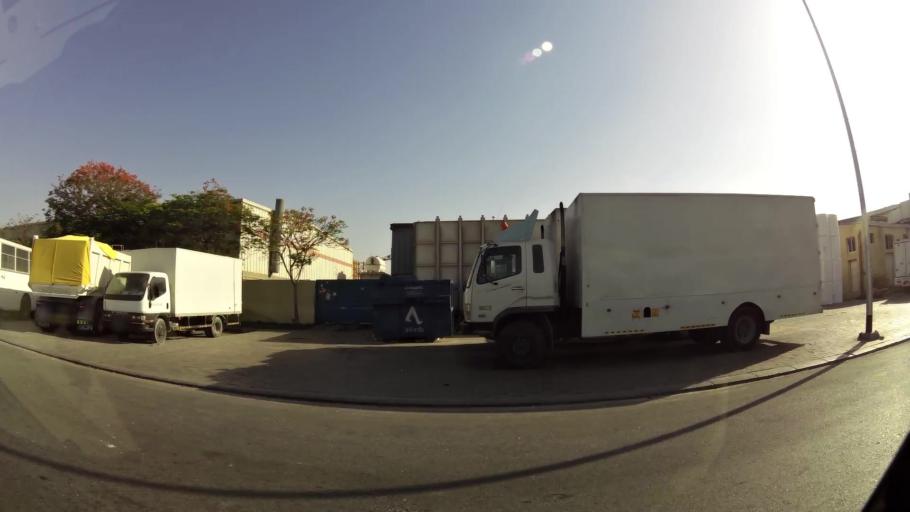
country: AE
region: Dubai
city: Dubai
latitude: 25.1237
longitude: 55.2342
